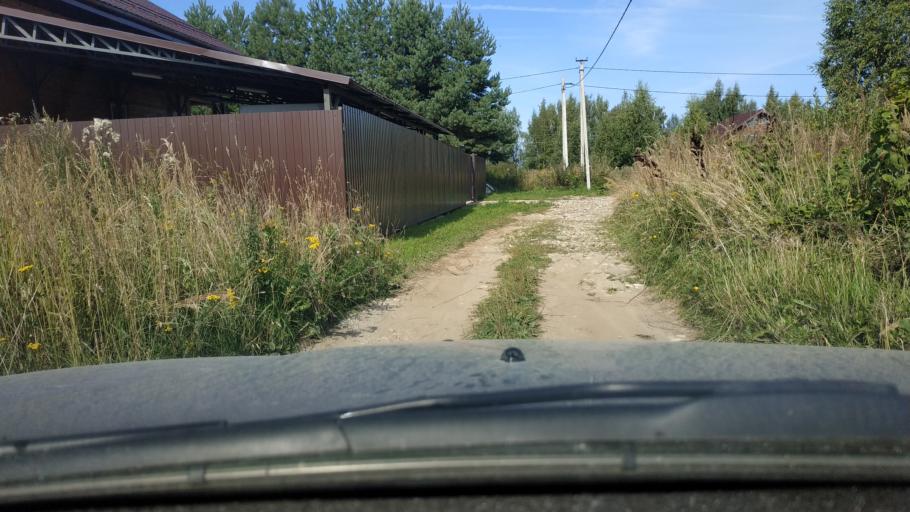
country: RU
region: Kostroma
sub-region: Kostromskoy Rayon
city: Kostroma
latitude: 57.7813
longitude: 40.7550
